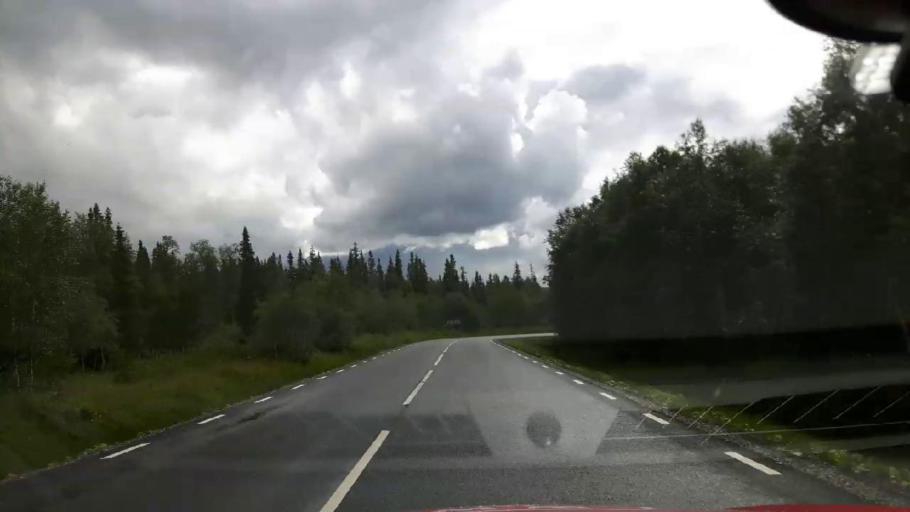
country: NO
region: Nord-Trondelag
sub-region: Royrvik
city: Royrvik
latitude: 64.8792
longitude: 14.2135
